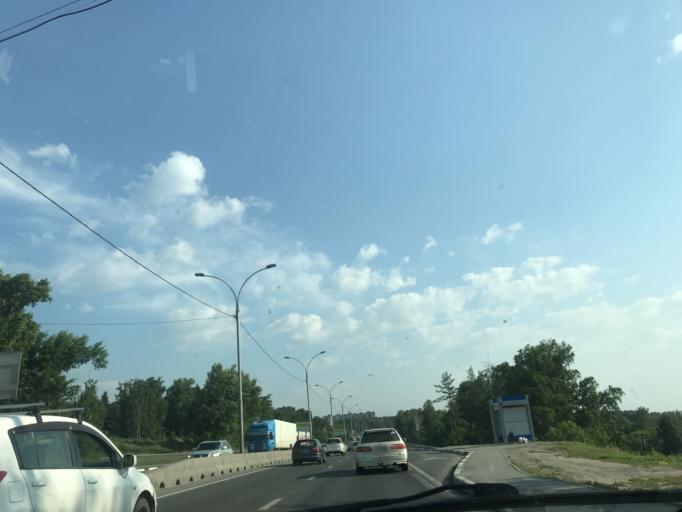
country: RU
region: Novosibirsk
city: Akademgorodok
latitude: 54.8147
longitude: 83.0890
